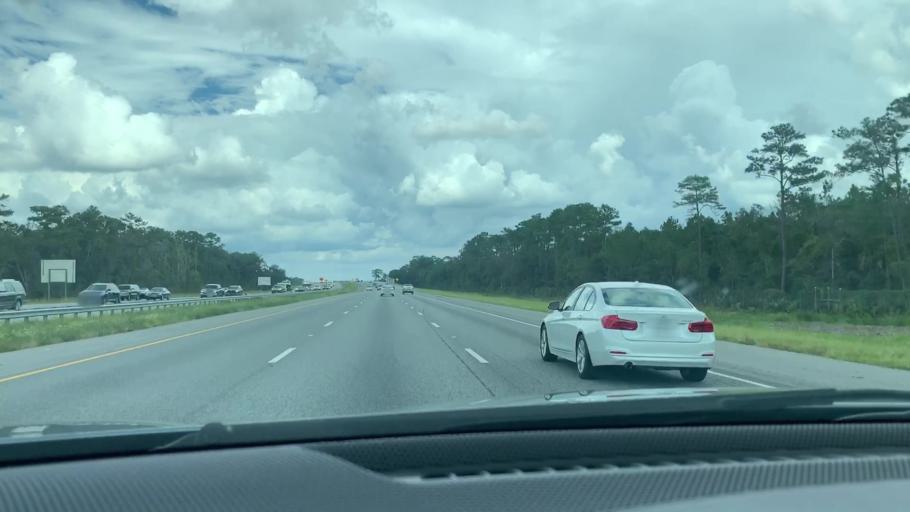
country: US
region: Georgia
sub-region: Glynn County
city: Dock Junction
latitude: 31.1599
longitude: -81.5584
